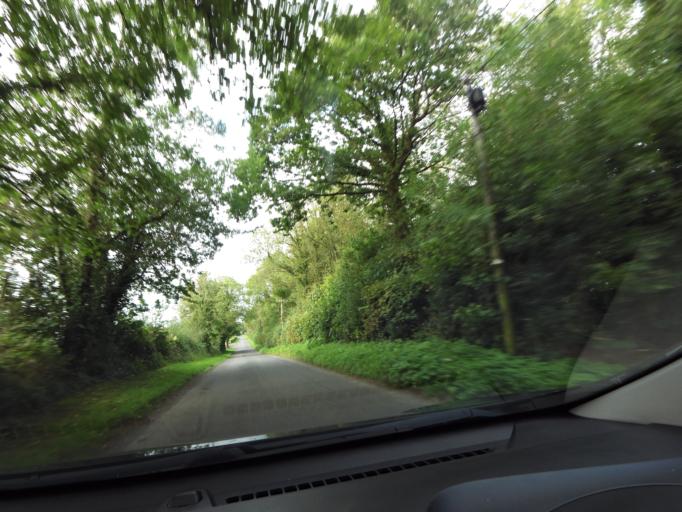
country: IE
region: Connaught
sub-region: County Galway
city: Ballinasloe
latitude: 53.3215
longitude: -8.1033
